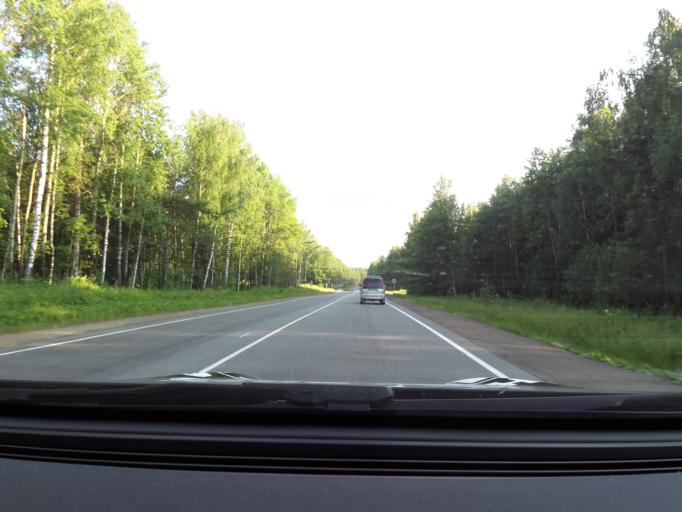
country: RU
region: Sverdlovsk
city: Druzhinino
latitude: 56.7527
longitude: 59.4645
